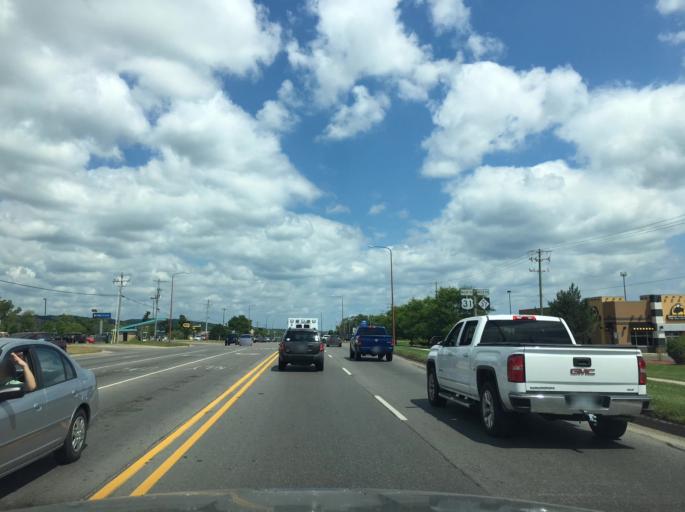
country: US
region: Michigan
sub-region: Grand Traverse County
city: Traverse City
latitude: 44.7231
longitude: -85.6460
